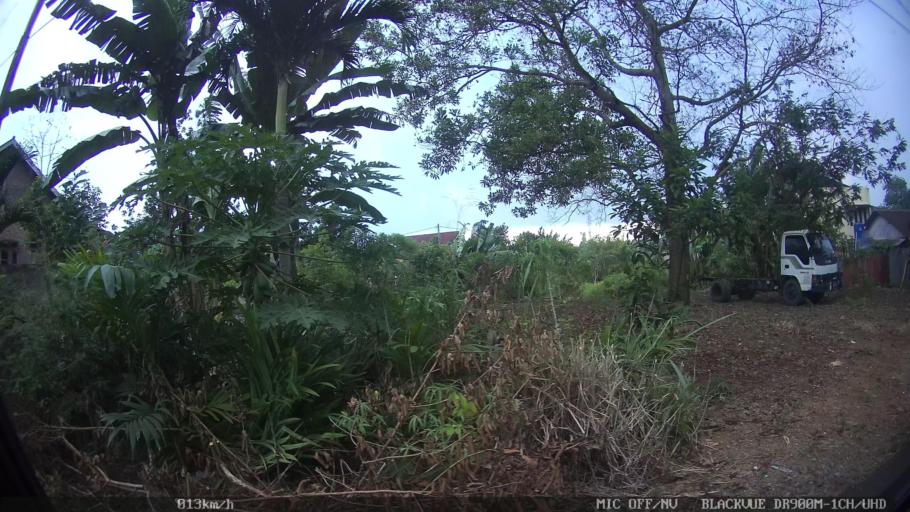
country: ID
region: Lampung
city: Kedaton
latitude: -5.3530
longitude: 105.2453
